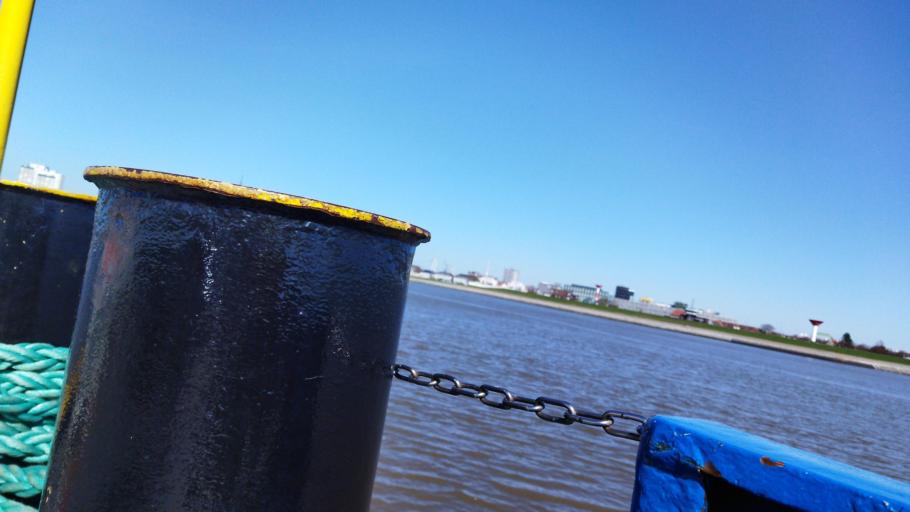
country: DE
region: Bremen
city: Bremerhaven
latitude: 53.5311
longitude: 8.5696
